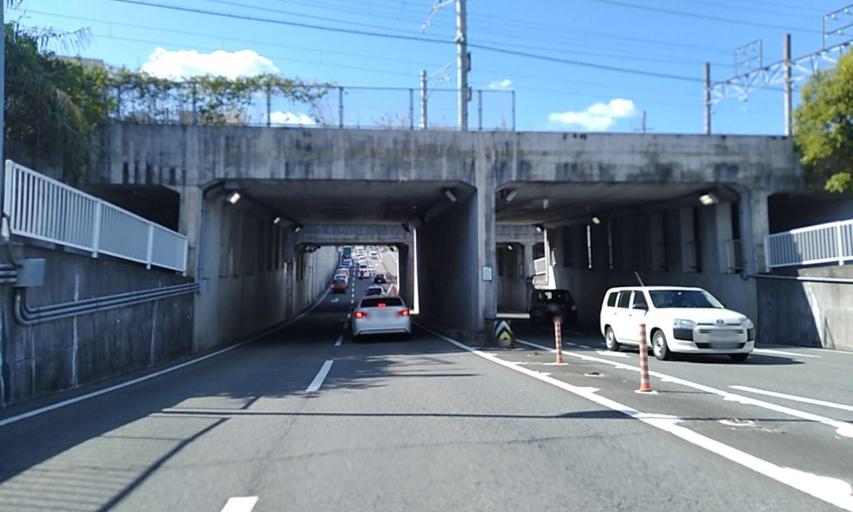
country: JP
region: Wakayama
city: Wakayama-shi
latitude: 34.2010
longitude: 135.1875
